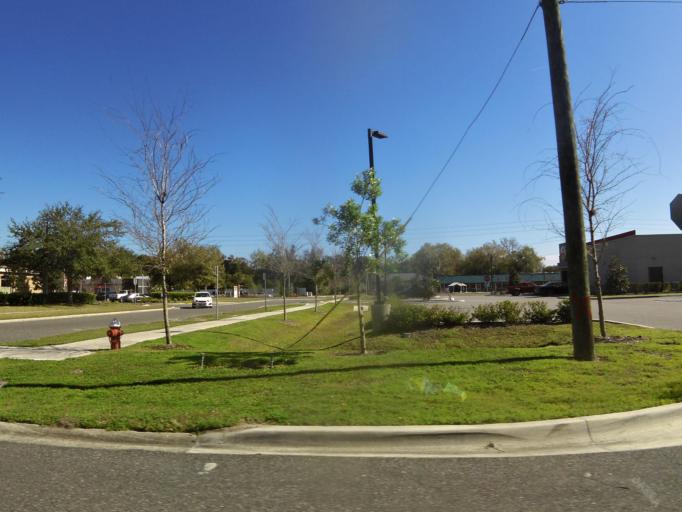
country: US
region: Florida
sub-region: Clay County
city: Green Cove Springs
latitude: 29.9985
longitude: -81.6832
